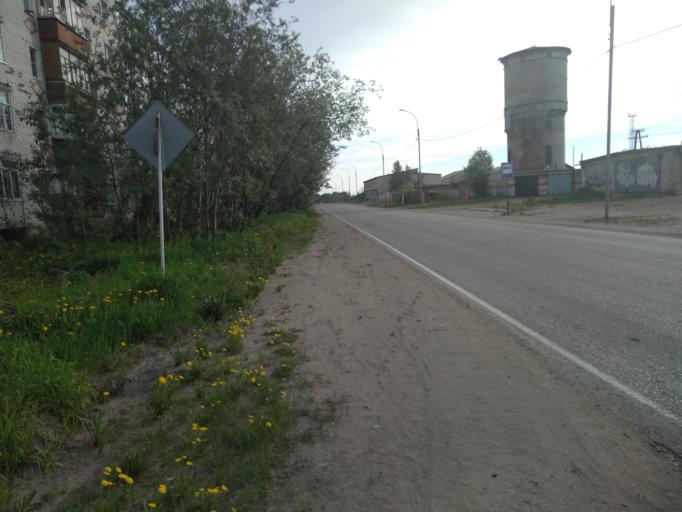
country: RU
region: Komi Republic
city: Pechora
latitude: 65.1483
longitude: 57.2137
